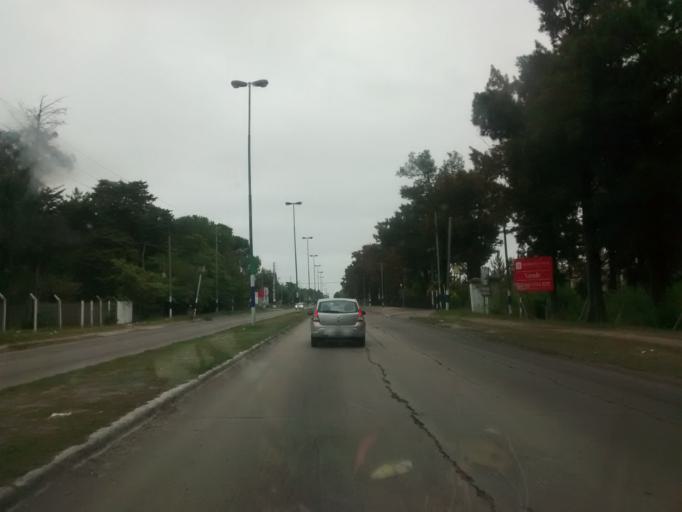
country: AR
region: Buenos Aires
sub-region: Partido de La Plata
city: La Plata
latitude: -34.9576
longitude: -58.0068
